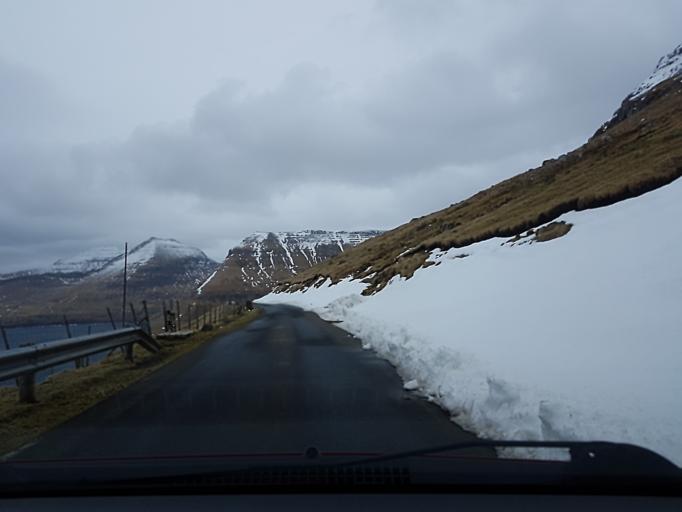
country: FO
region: Streymoy
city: Kollafjordhur
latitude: 62.0084
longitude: -6.9093
